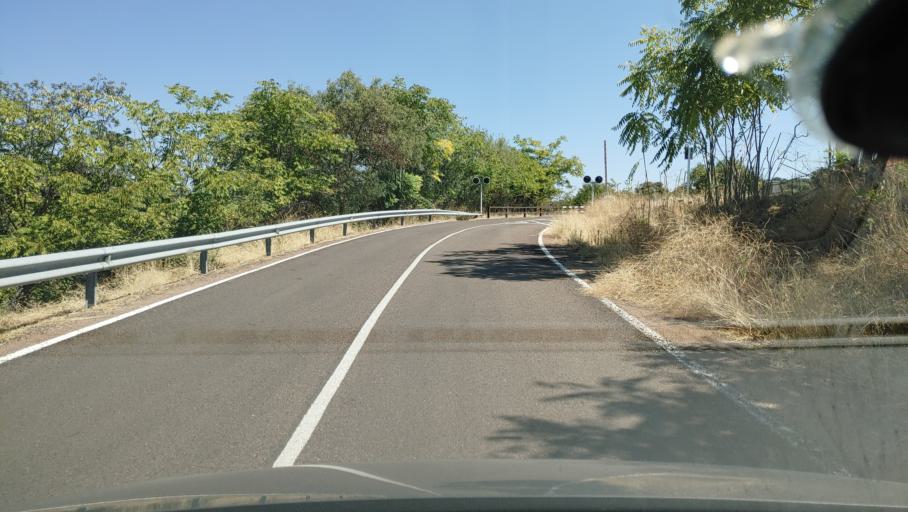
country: ES
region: Castille-La Mancha
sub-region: Provincia de Ciudad Real
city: Alamillo
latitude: 38.7408
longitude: -4.7278
